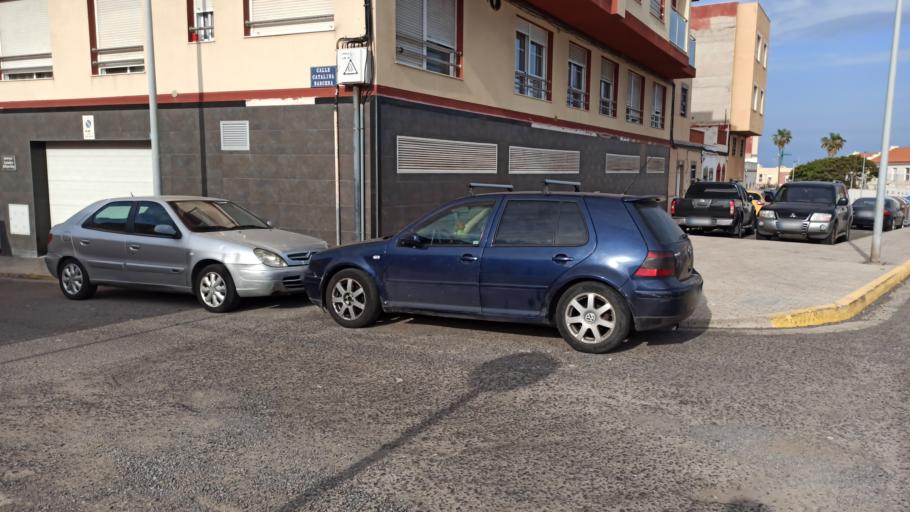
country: ES
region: Melilla
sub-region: Melilla
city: Melilla
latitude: 35.2824
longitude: -2.9466
